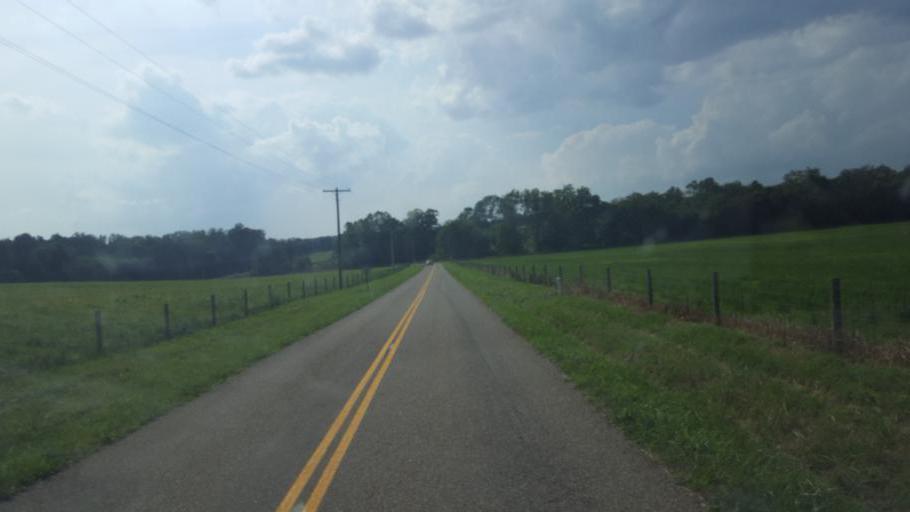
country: US
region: Ohio
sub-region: Knox County
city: Gambier
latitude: 40.3356
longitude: -82.3776
